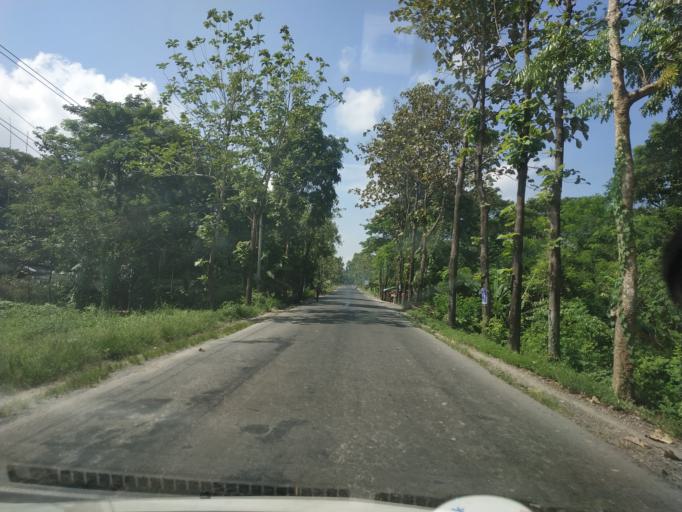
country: MM
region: Ayeyarwady
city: Nyaungdon
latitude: 17.0418
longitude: 95.5404
